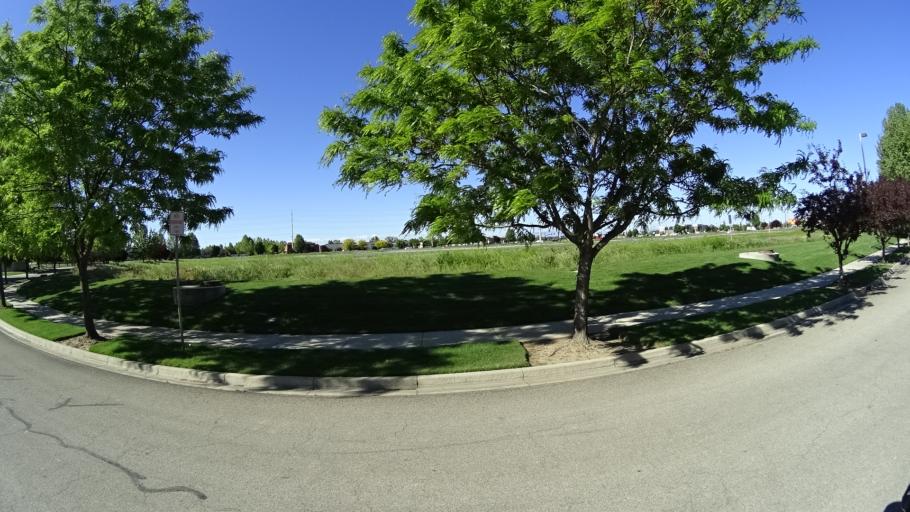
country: US
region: Idaho
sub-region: Ada County
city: Meridian
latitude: 43.6507
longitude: -116.4305
